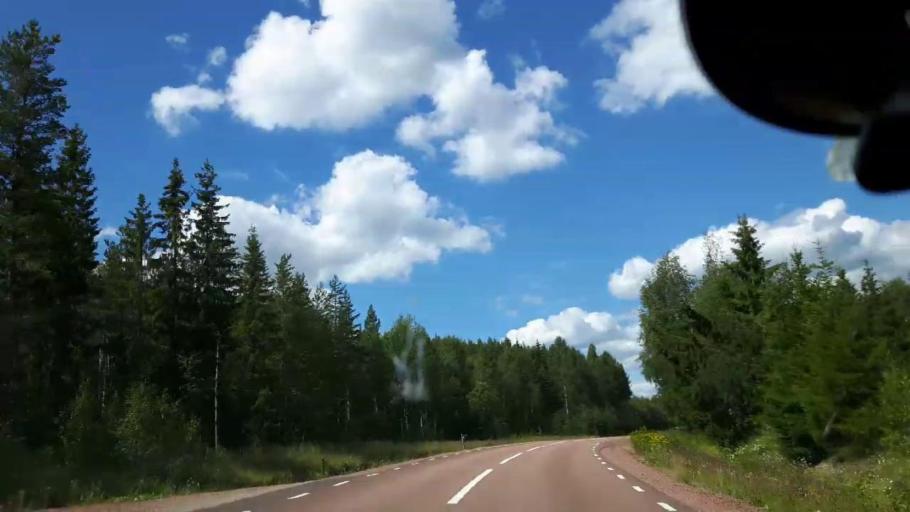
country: SE
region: Jaemtland
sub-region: Ragunda Kommun
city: Hammarstrand
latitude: 63.0221
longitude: 16.5419
